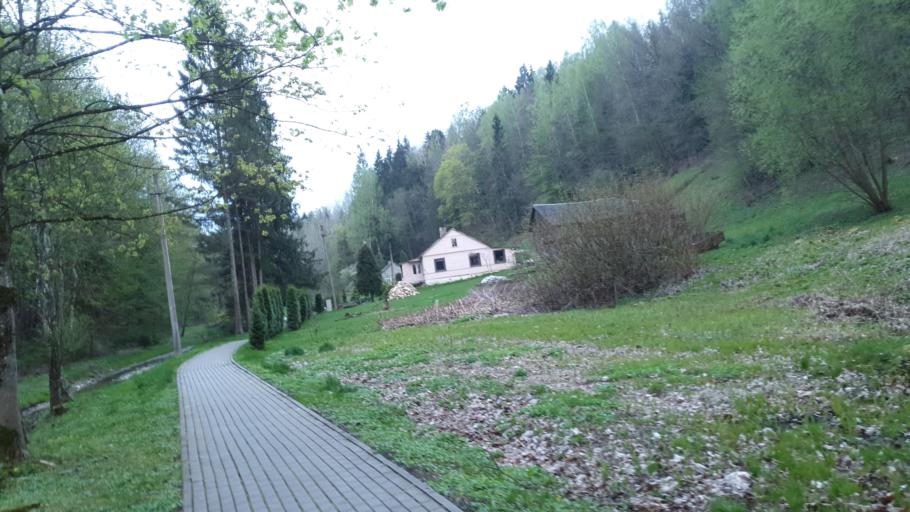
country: LT
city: Sakiai
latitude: 55.0811
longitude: 23.1781
